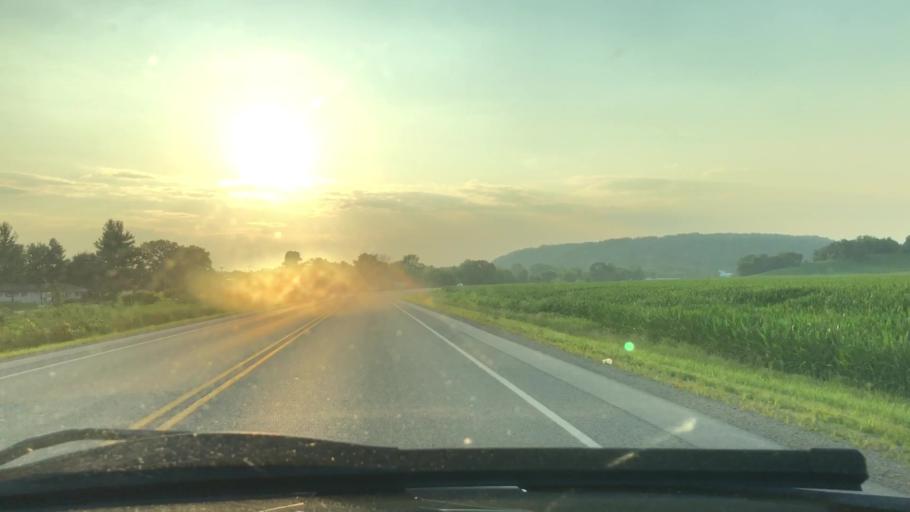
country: US
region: Wisconsin
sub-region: Dane County
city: Black Earth
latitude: 43.1361
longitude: -89.7361
